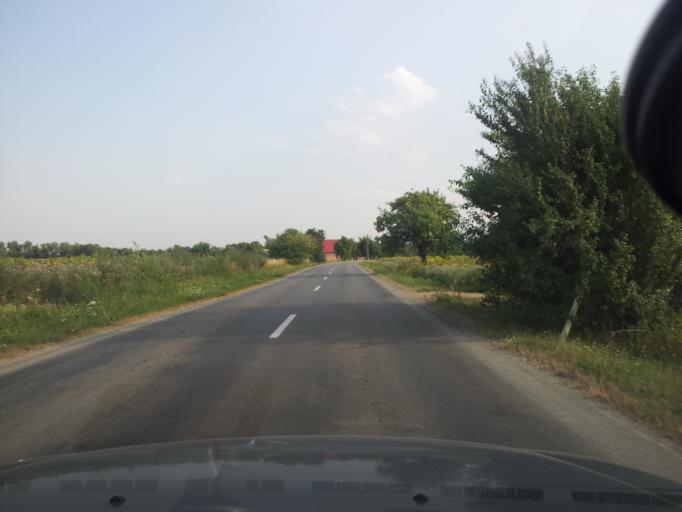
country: SK
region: Nitriansky
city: Banovce nad Bebravou
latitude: 48.7900
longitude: 18.1997
